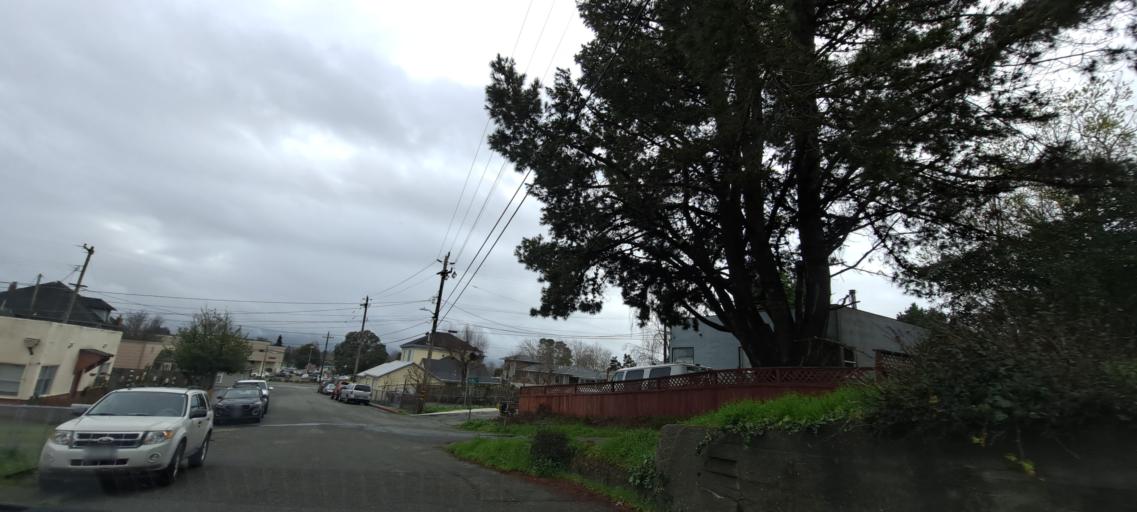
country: US
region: California
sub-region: Humboldt County
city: Fortuna
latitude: 40.5973
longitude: -124.1449
